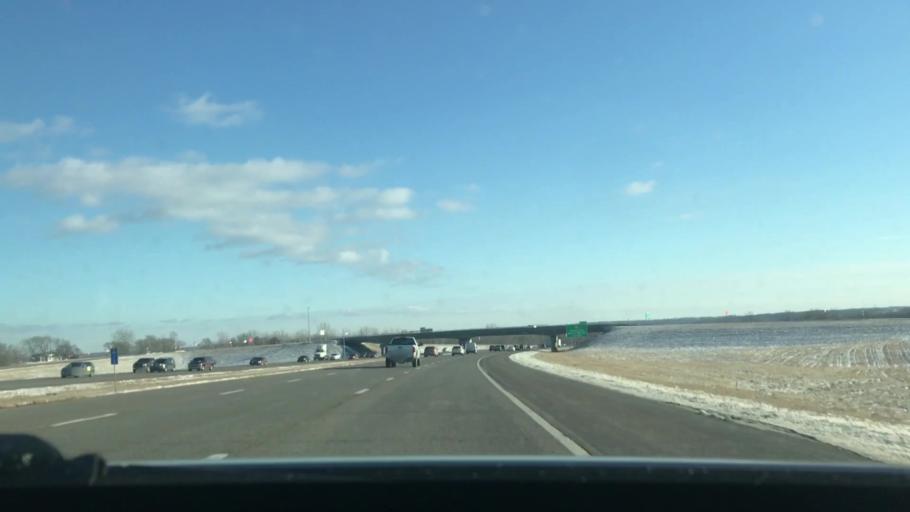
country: US
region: Kansas
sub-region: Wyandotte County
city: Edwardsville
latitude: 39.0898
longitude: -94.8026
